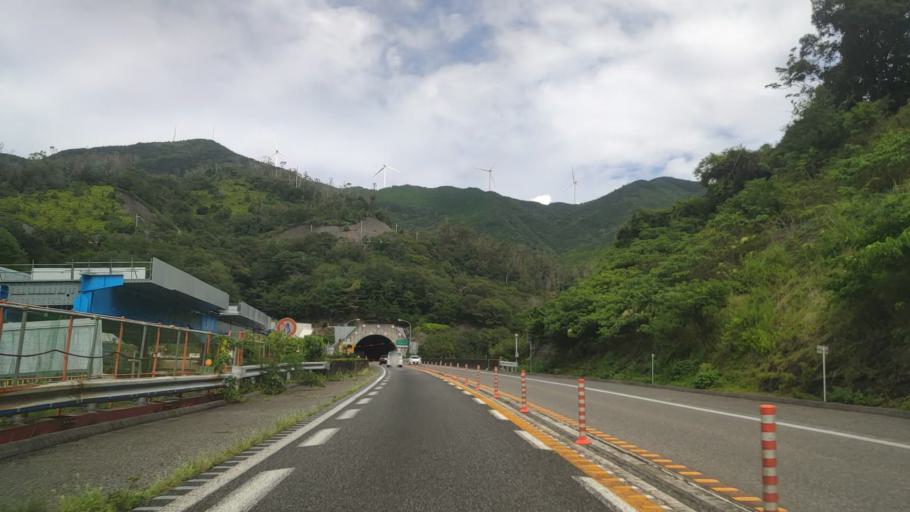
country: JP
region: Wakayama
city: Gobo
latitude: 33.9418
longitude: 135.1984
